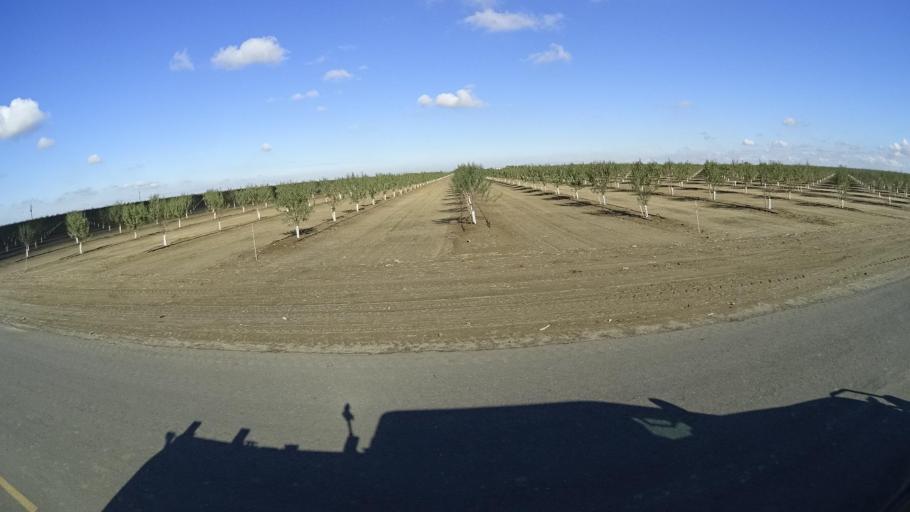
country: US
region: California
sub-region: Kern County
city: McFarland
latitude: 35.6598
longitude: -119.2569
